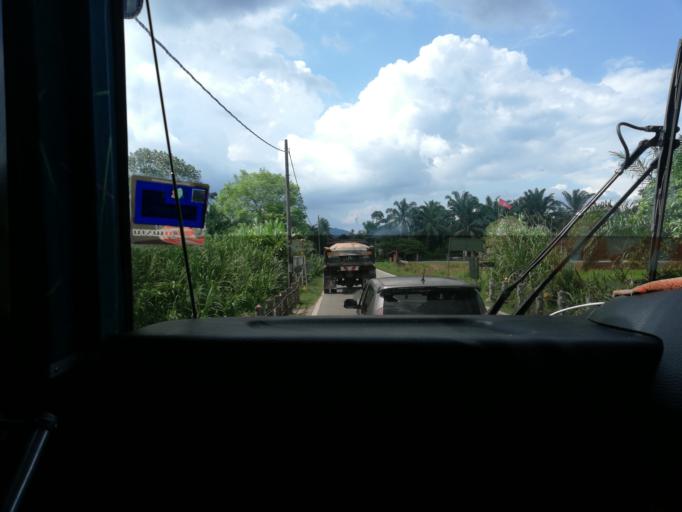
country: MY
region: Penang
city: Nibong Tebal
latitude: 5.2241
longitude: 100.6075
